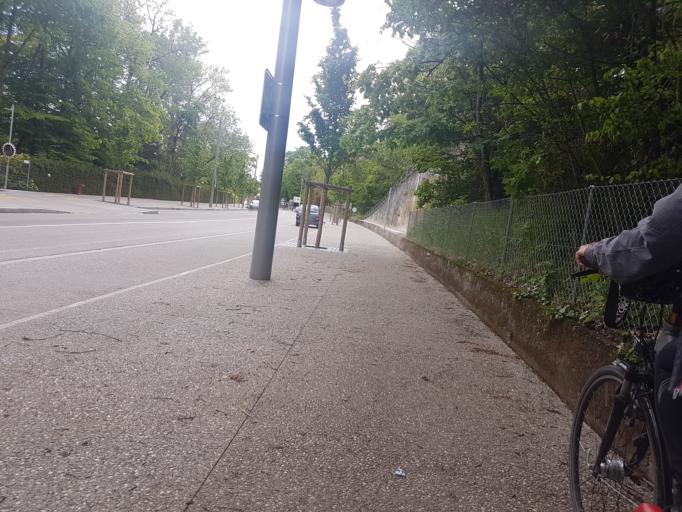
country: CH
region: Geneva
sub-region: Geneva
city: Versoix
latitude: 46.2940
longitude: 6.1661
